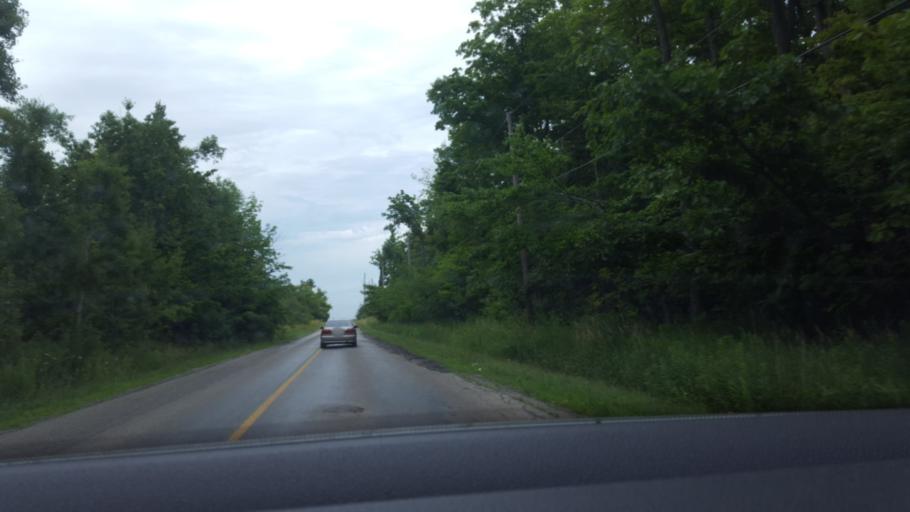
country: CA
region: Ontario
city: Brampton
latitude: 43.6136
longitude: -79.8403
